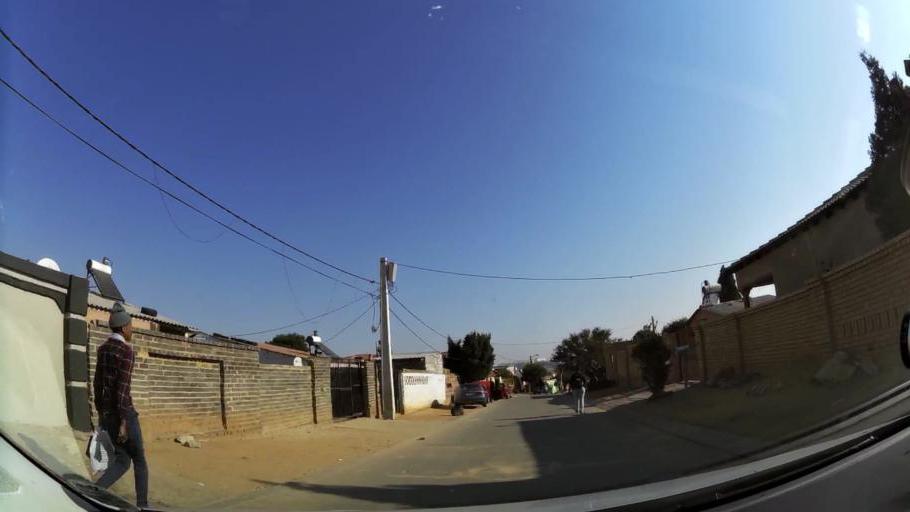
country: ZA
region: Gauteng
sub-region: City of Johannesburg Metropolitan Municipality
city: Modderfontein
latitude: -26.1037
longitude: 28.1151
